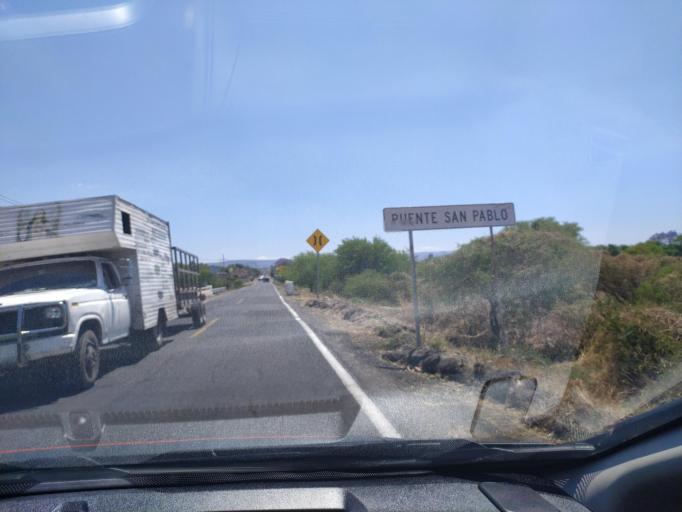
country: MX
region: Guanajuato
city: Ciudad Manuel Doblado
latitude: 20.7539
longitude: -101.8261
